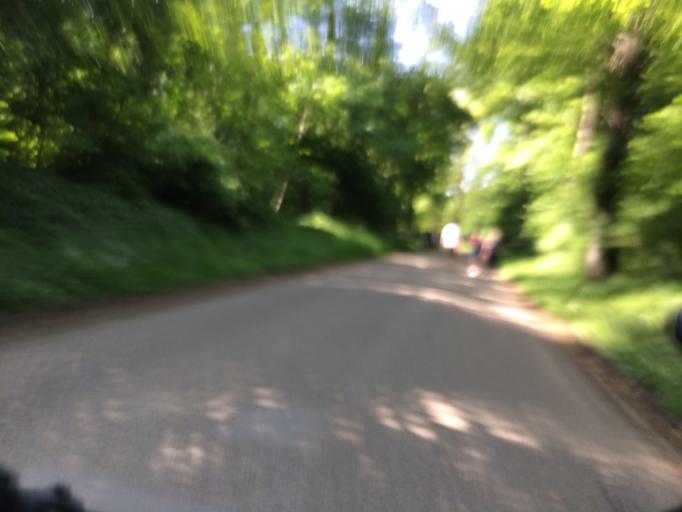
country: FR
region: Ile-de-France
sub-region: Departement des Hauts-de-Seine
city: Chatenay-Malabry
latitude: 48.7587
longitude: 2.2448
